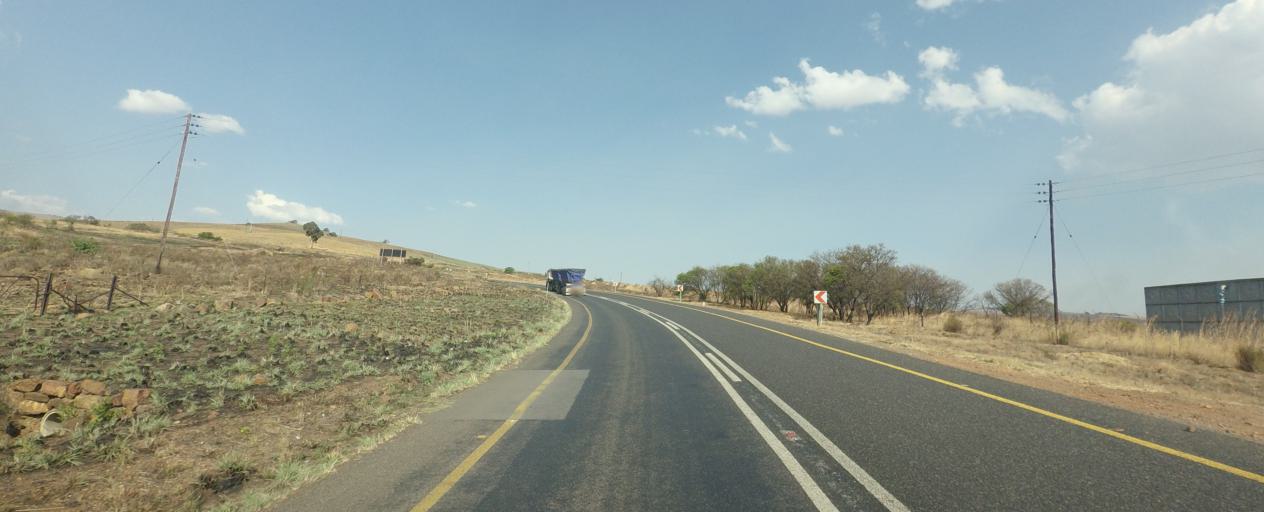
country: ZA
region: Mpumalanga
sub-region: Ehlanzeni District
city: Lydenburg
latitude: -25.1098
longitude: 30.4956
